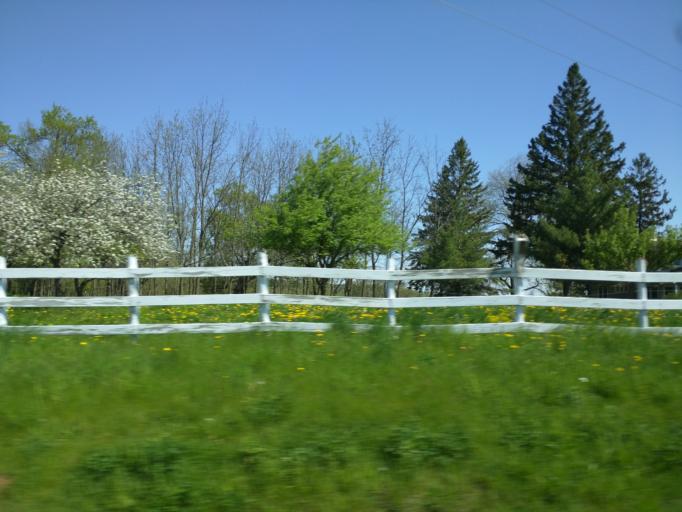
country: US
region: Wisconsin
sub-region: Monroe County
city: Cashton
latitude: 43.6818
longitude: -90.6511
